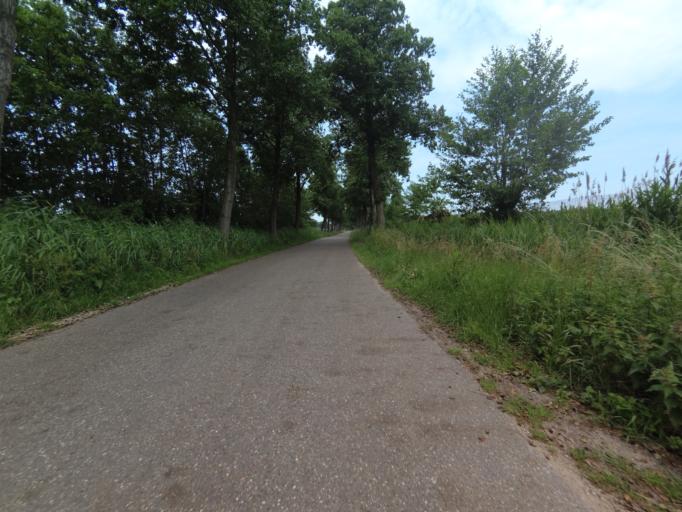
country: NL
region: Gelderland
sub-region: Gemeente Ede
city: Lunteren
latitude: 52.0612
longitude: 5.6300
